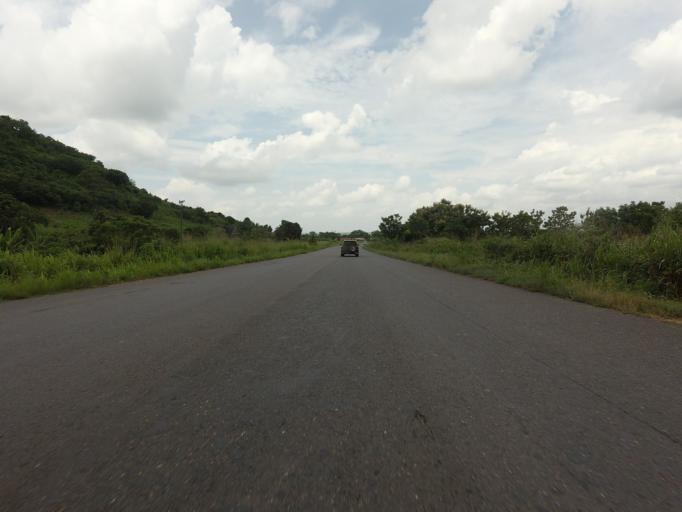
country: GH
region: Volta
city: Ho
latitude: 6.4229
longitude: 0.1709
